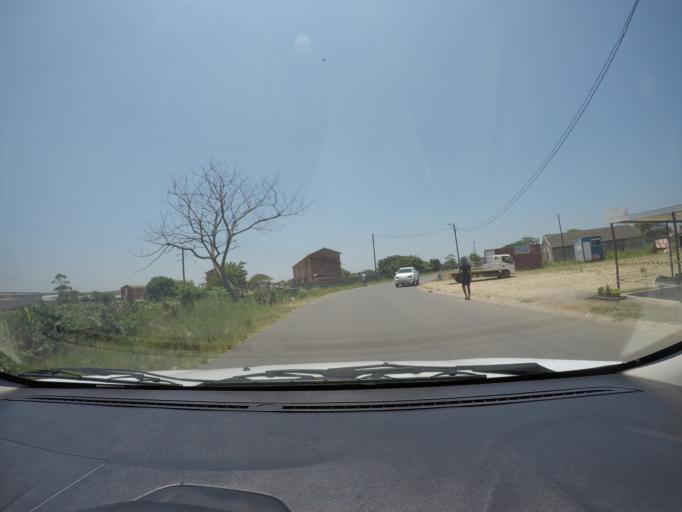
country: ZA
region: KwaZulu-Natal
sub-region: uThungulu District Municipality
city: eSikhawini
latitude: -28.8756
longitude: 31.9005
